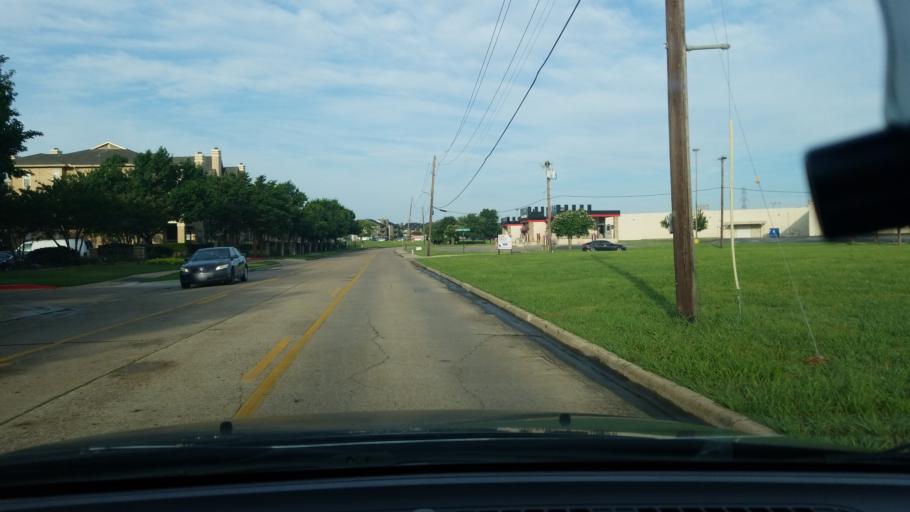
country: US
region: Texas
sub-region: Dallas County
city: Mesquite
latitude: 32.8078
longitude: -96.6137
